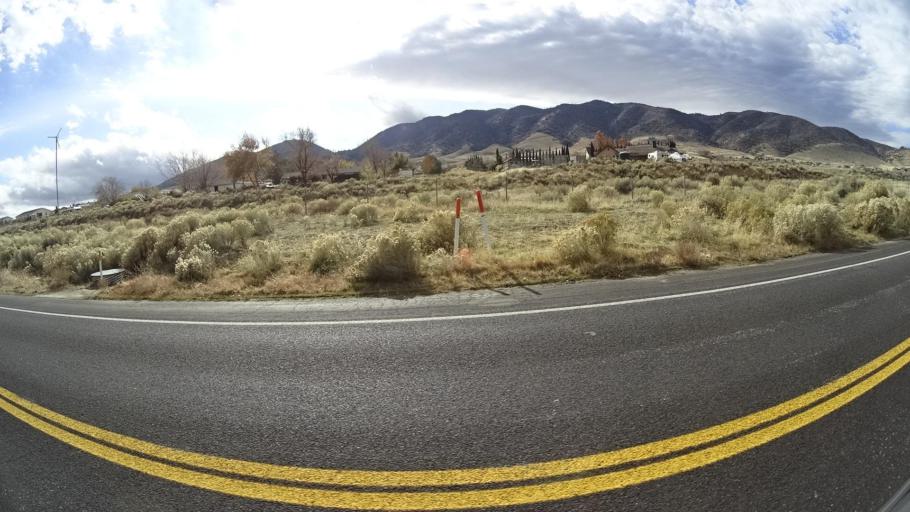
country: US
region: California
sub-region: Kern County
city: Tehachapi
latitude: 35.1106
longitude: -118.4563
